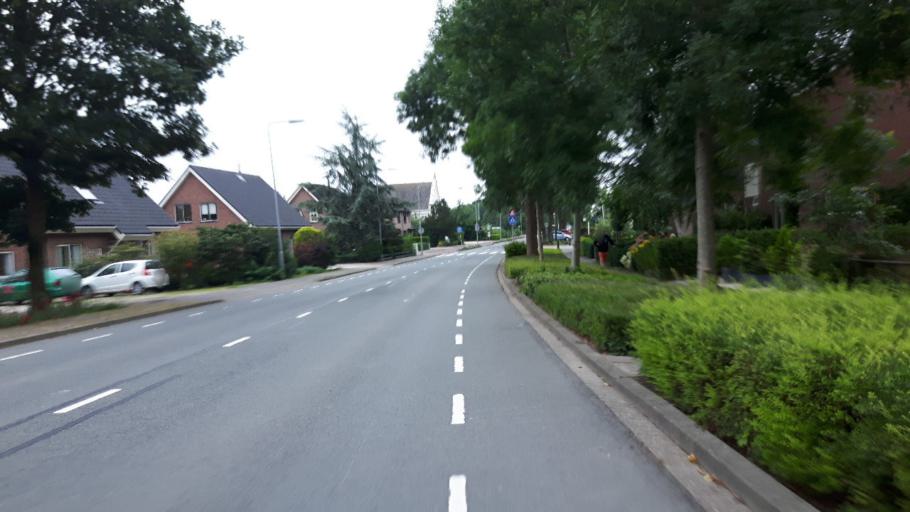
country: NL
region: South Holland
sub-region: Gemeente Nieuwkoop
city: Nieuwkoop
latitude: 52.1799
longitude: 4.7823
